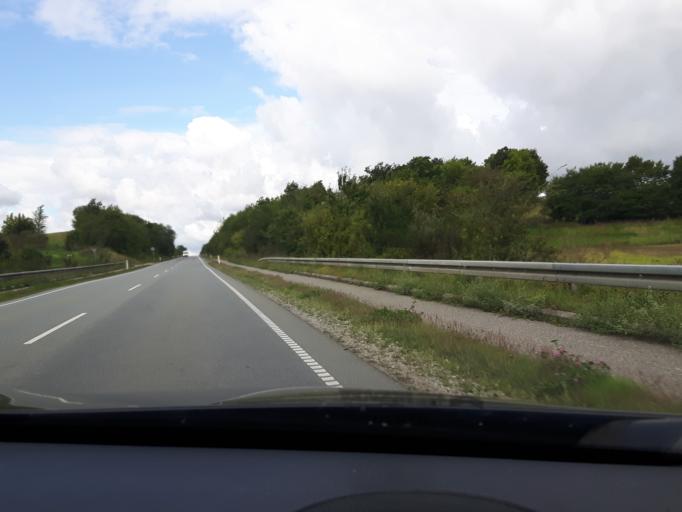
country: DK
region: Central Jutland
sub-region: Hedensted Kommune
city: Hedensted
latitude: 55.7202
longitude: 9.7281
